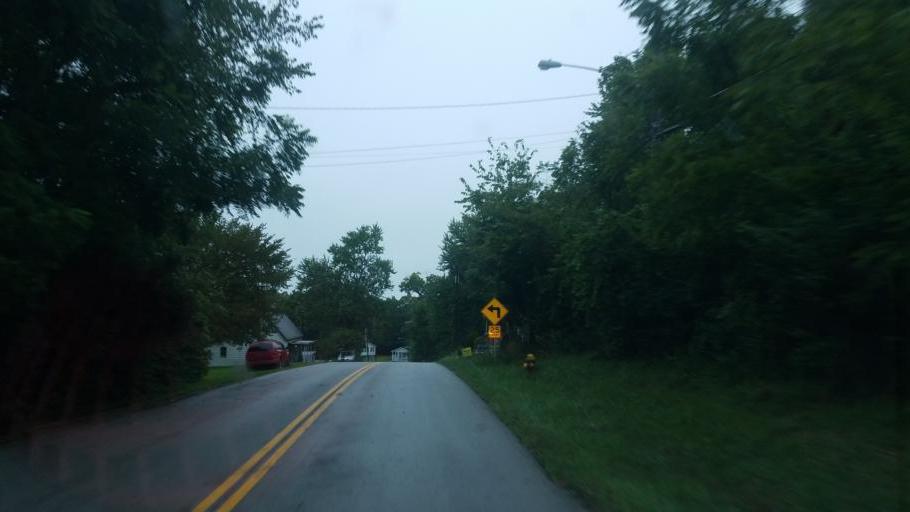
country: US
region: Kentucky
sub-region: Fleming County
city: Flemingsburg
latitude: 38.4269
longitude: -83.7231
